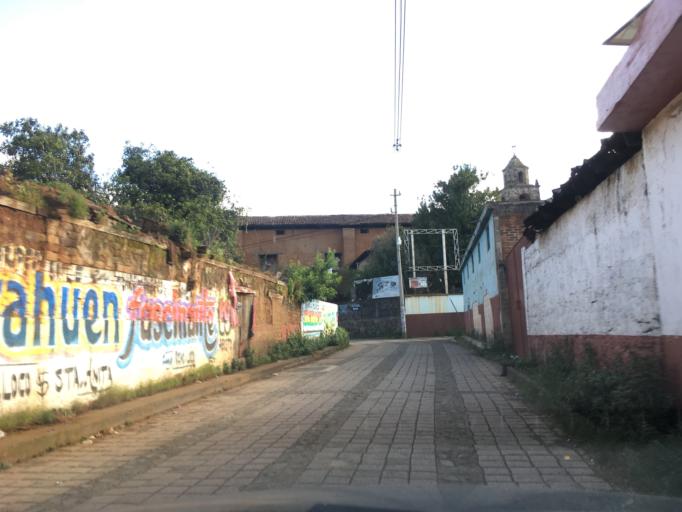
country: MX
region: Michoacan
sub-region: Patzcuaro
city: Santa Maria Huiramangaro (San Juan Tumbio)
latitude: 19.4538
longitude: -101.7308
